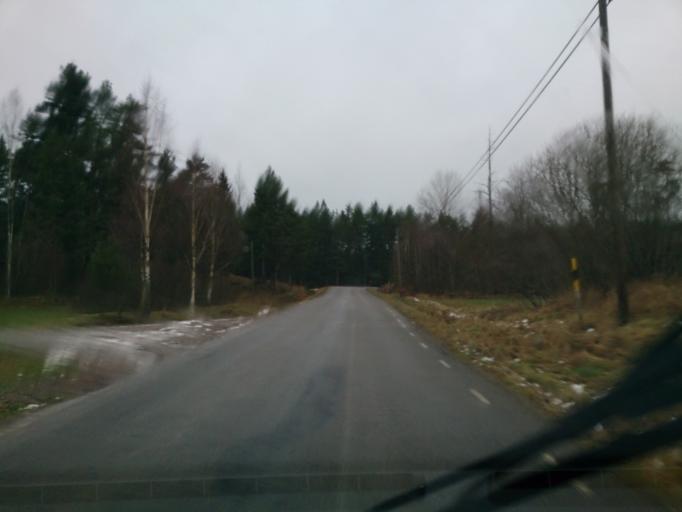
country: SE
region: OEstergoetland
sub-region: Atvidabergs Kommun
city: Atvidaberg
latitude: 58.2225
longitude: 16.0506
